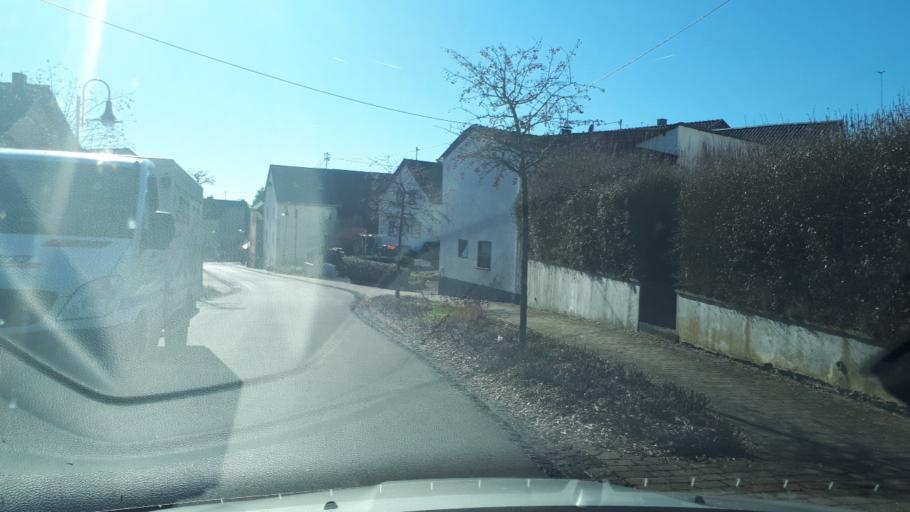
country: DE
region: Rheinland-Pfalz
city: Ellscheid
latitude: 50.1522
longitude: 6.9152
